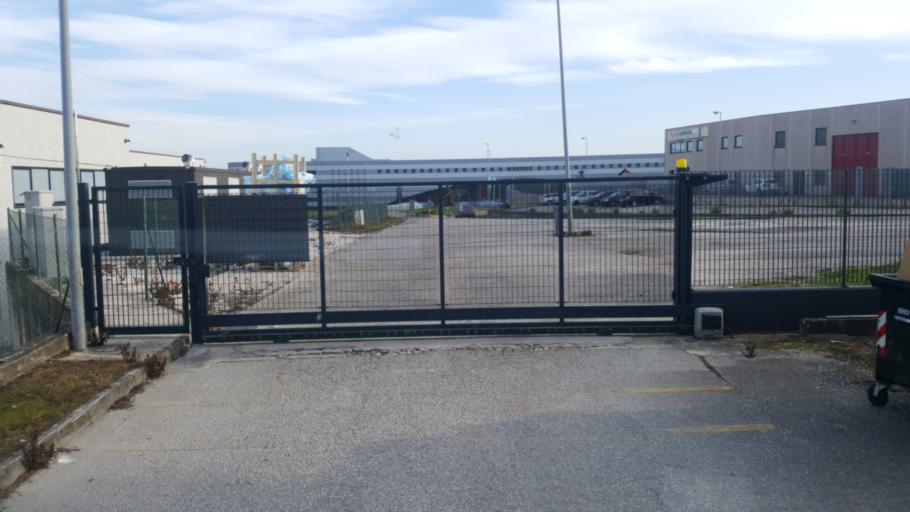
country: IT
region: The Marches
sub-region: Provincia di Pesaro e Urbino
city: Mondolfo
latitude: 43.7477
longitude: 13.1178
